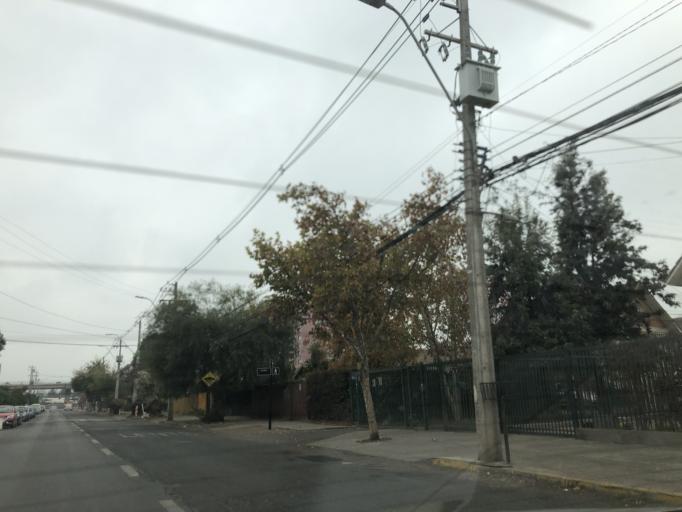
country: CL
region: Santiago Metropolitan
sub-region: Provincia de Cordillera
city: Puente Alto
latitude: -33.5862
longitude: -70.5832
